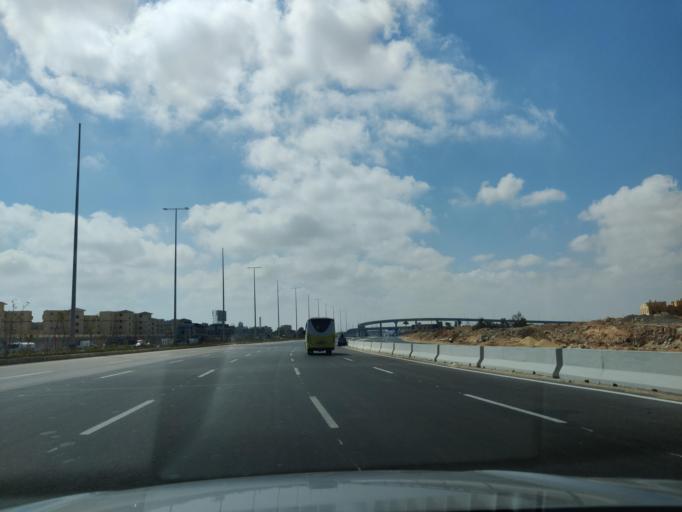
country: EG
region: Muhafazat Matruh
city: Al `Alamayn
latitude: 30.9566
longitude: 28.7655
